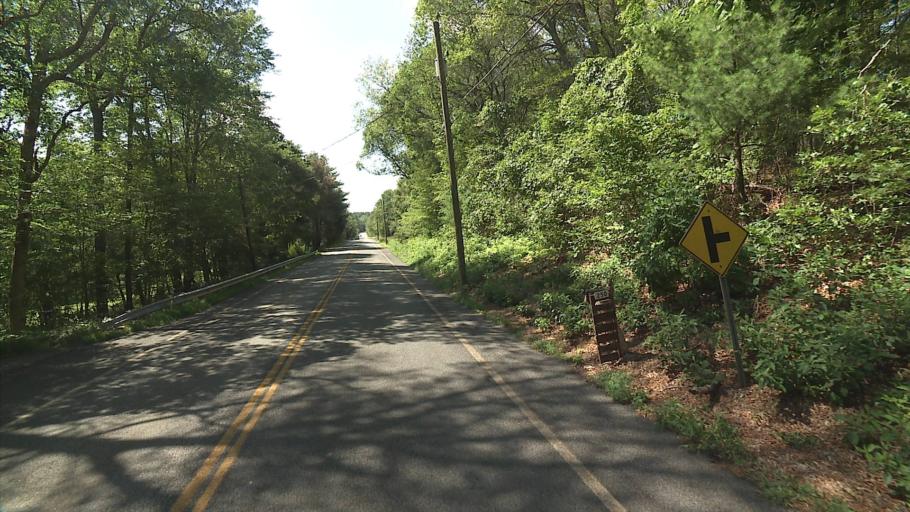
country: US
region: Connecticut
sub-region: Tolland County
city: Mansfield City
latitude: 41.7808
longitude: -72.1880
